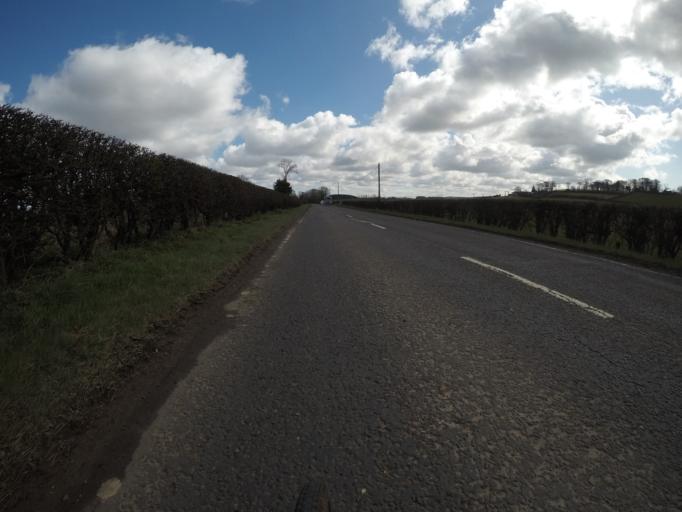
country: GB
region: Scotland
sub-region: South Ayrshire
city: Dundonald
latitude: 55.5862
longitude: -4.5727
